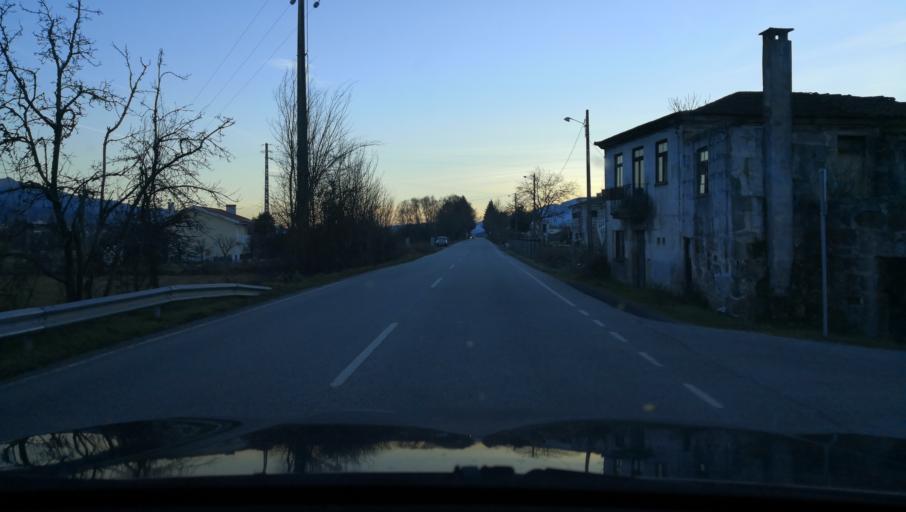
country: PT
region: Vila Real
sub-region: Vila Pouca de Aguiar
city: Vila Pouca de Aguiar
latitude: 41.4758
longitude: -7.6587
